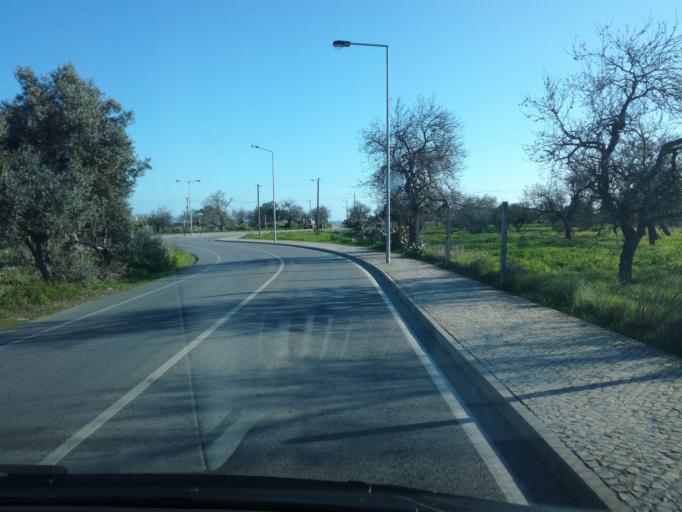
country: PT
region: Faro
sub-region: Olhao
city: Laranjeiro
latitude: 37.0543
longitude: -7.7583
